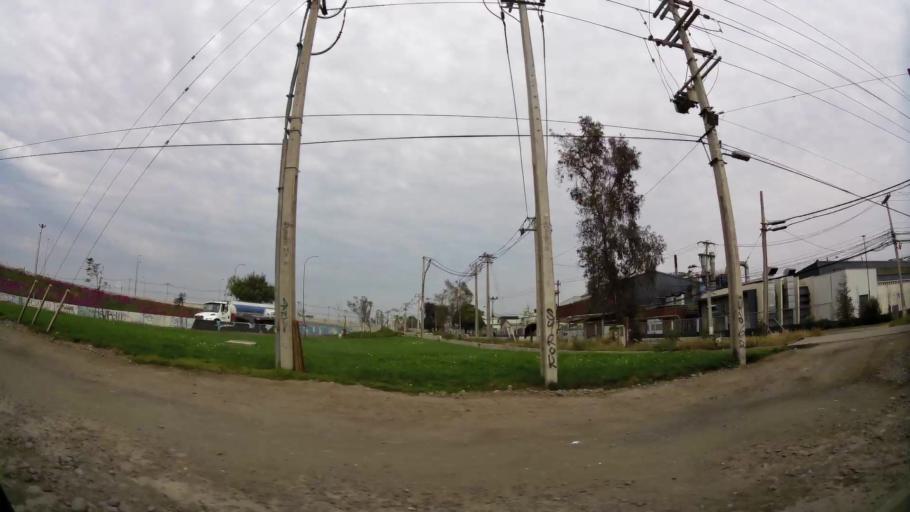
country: CL
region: Santiago Metropolitan
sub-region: Provincia de Maipo
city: San Bernardo
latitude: -33.5286
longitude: -70.7585
